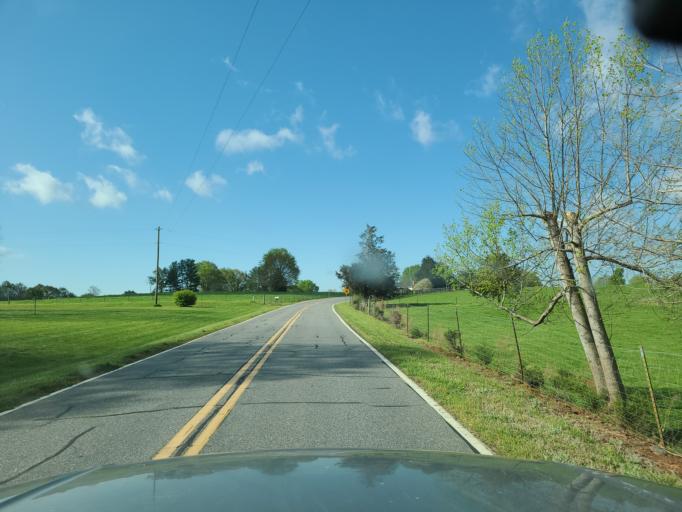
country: US
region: North Carolina
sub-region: Rutherford County
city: Forest City
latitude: 35.4263
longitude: -81.8528
